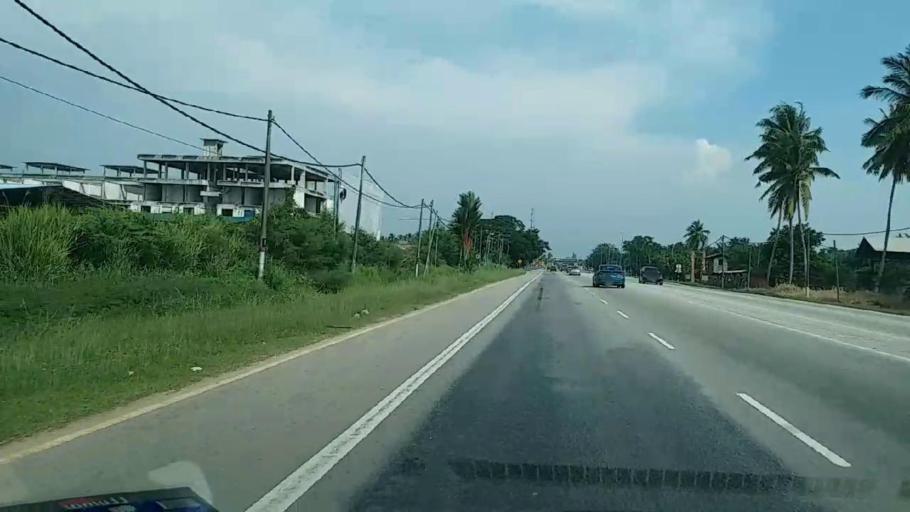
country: MY
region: Selangor
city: Kuala Selangor
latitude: 3.3673
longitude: 101.2439
